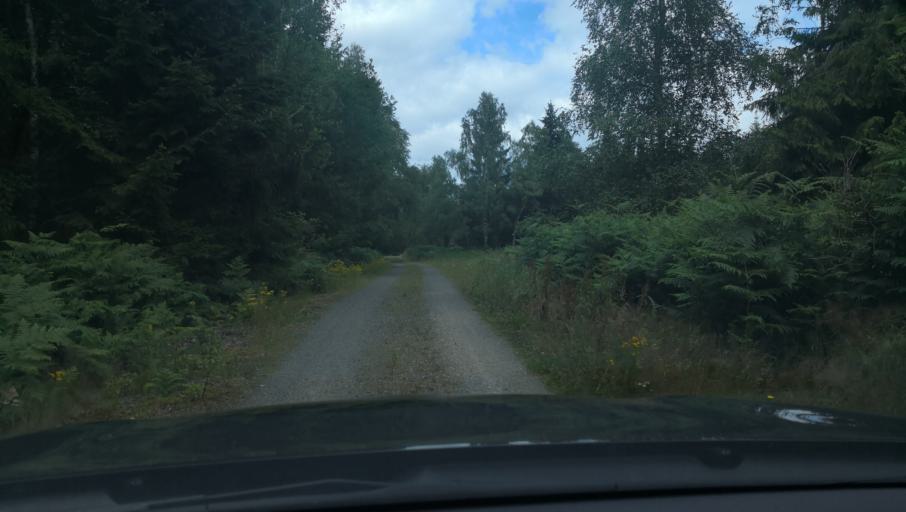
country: SE
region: Skane
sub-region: Simrishamns Kommun
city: Kivik
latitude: 55.6116
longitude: 14.1070
